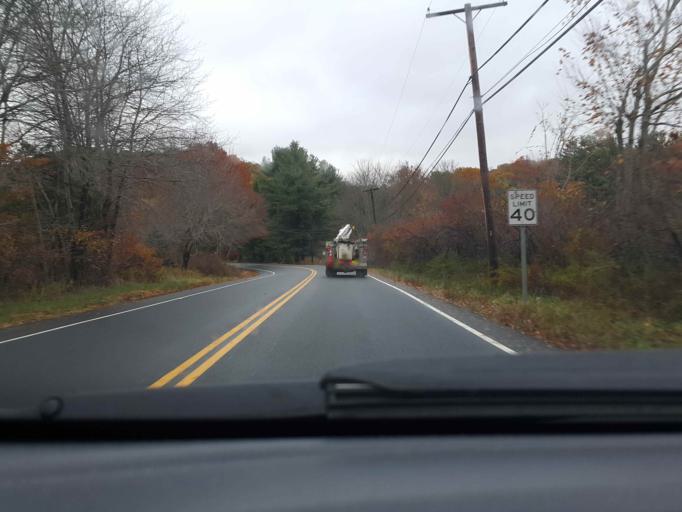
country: US
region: Connecticut
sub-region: Middlesex County
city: Durham
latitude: 41.4175
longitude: -72.6900
